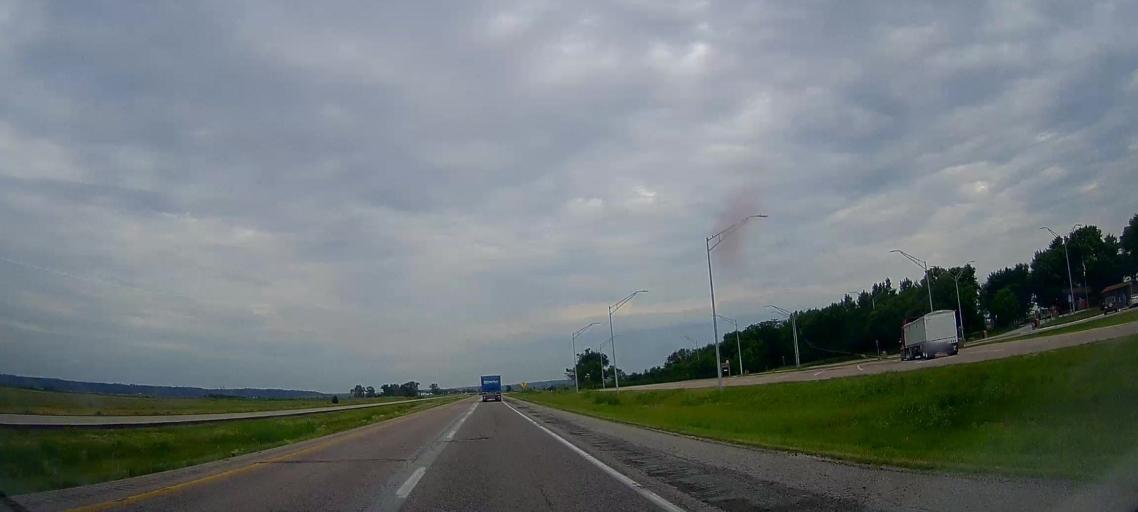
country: US
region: Iowa
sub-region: Harrison County
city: Missouri Valley
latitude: 41.5923
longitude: -95.9532
